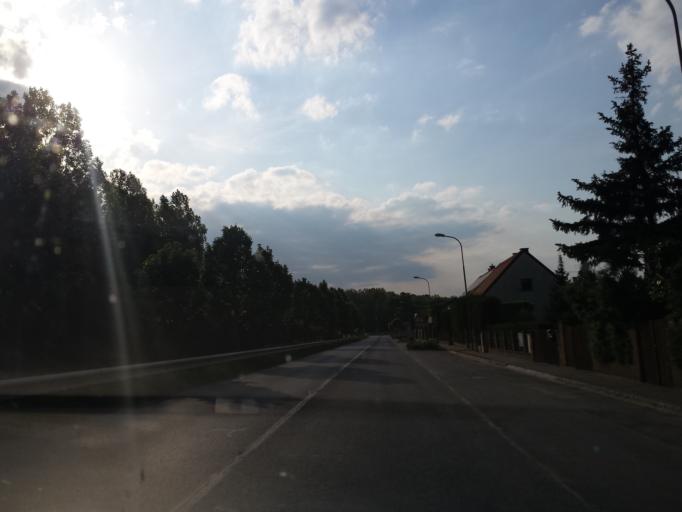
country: AT
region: Lower Austria
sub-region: Politischer Bezirk Ganserndorf
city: Obersiebenbrunn
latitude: 48.2668
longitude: 16.7177
